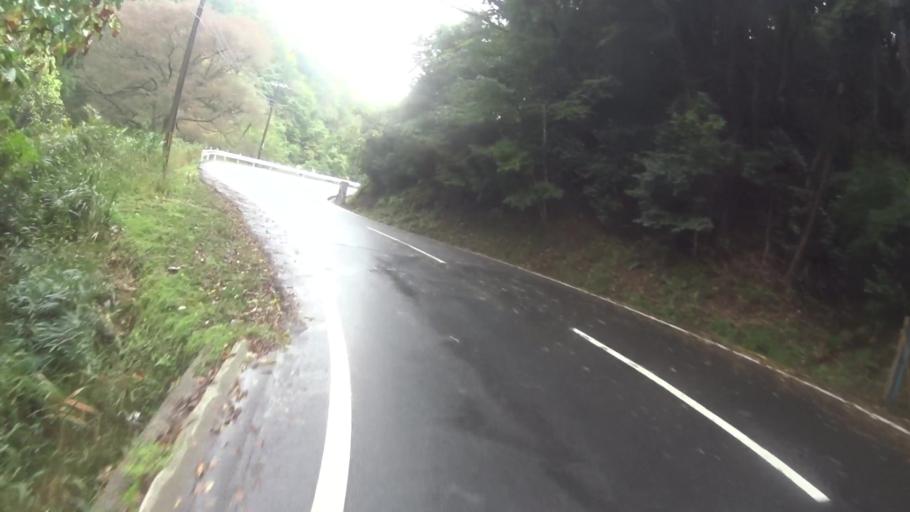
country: JP
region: Kyoto
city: Miyazu
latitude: 35.5269
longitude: 135.0508
